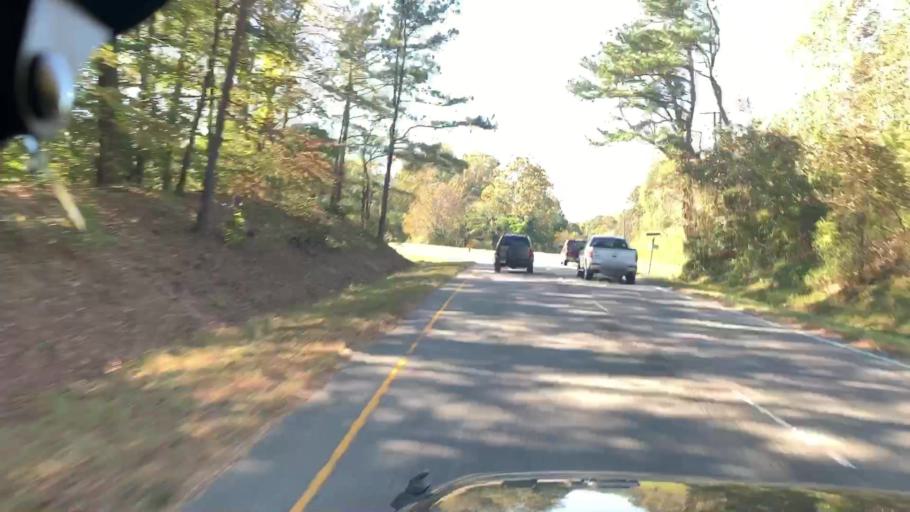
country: US
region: Virginia
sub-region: James City County
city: Williamsburg
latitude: 37.3743
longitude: -76.7817
